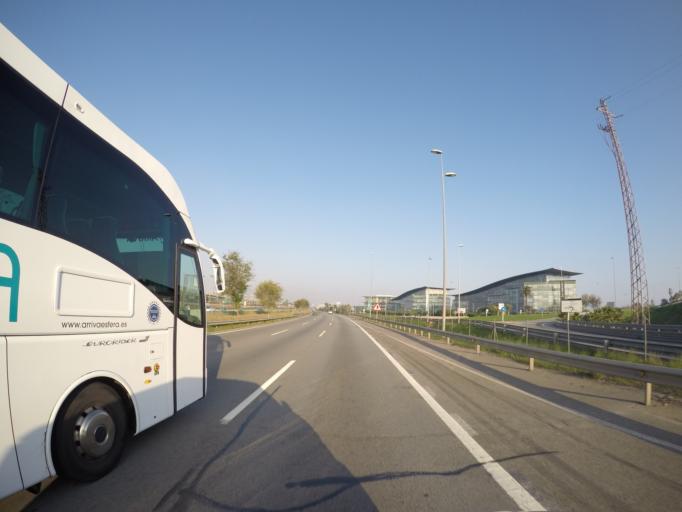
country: ES
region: Catalonia
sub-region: Provincia de Barcelona
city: L'Hospitalet de Llobregat
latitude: 41.3400
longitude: 2.1207
